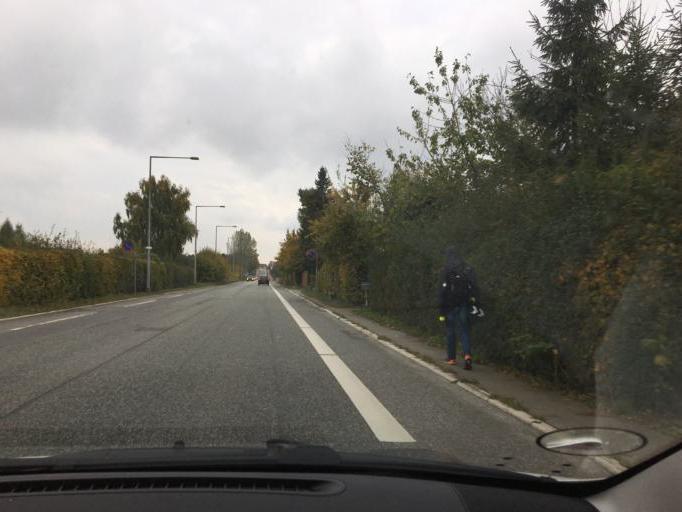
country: DK
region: South Denmark
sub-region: Fredericia Kommune
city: Fredericia
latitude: 55.5858
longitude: 9.7540
